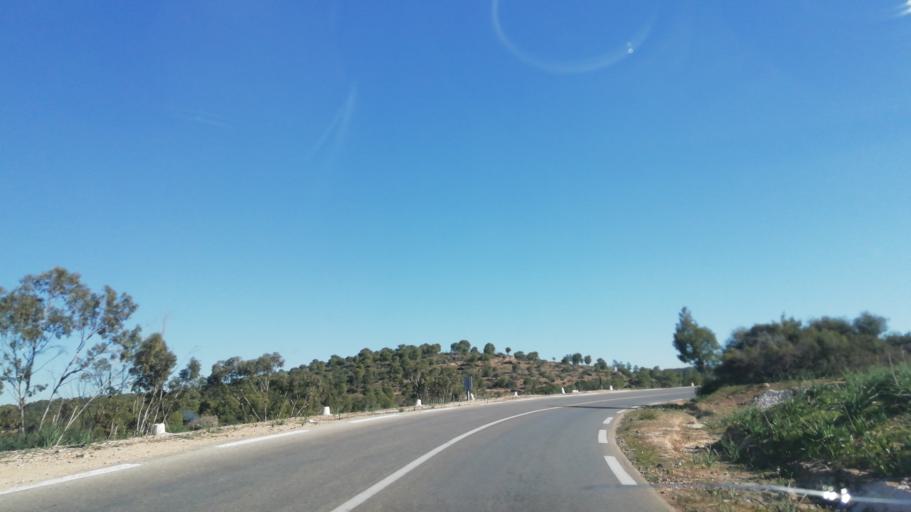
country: DZ
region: Tlemcen
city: Beni Mester
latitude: 34.8139
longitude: -1.6280
